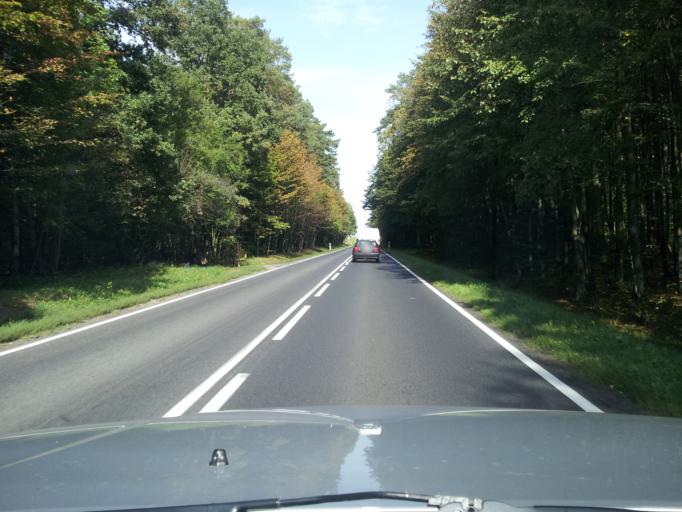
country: PL
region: Warmian-Masurian Voivodeship
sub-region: Powiat nowomiejski
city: Nowe Miasto Lubawskie
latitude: 53.4790
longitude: 19.6296
